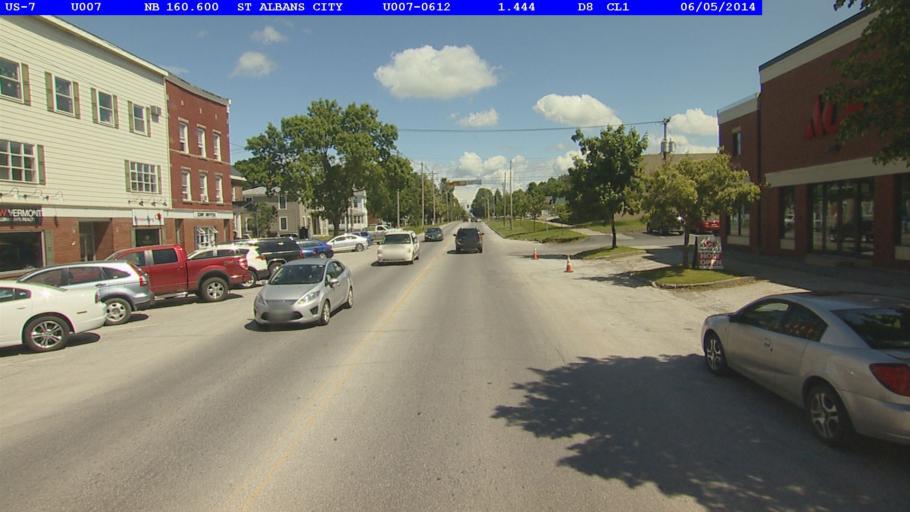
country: US
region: Vermont
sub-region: Franklin County
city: Saint Albans
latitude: 44.8136
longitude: -73.0829
